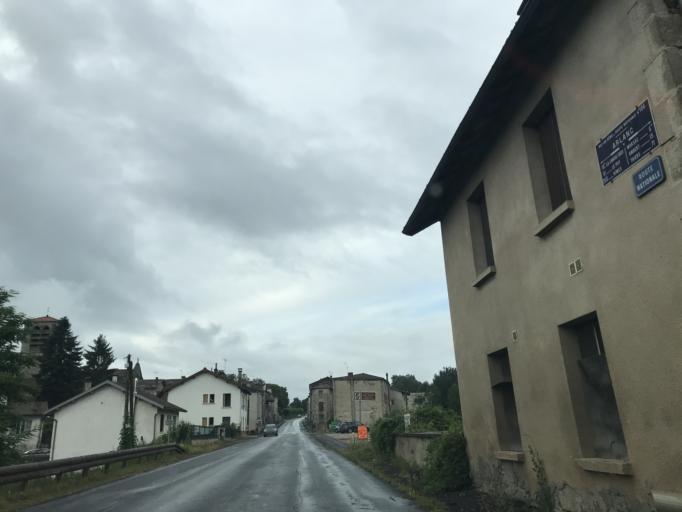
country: FR
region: Auvergne
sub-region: Departement du Puy-de-Dome
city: Arlanc
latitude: 45.4229
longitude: 3.7247
